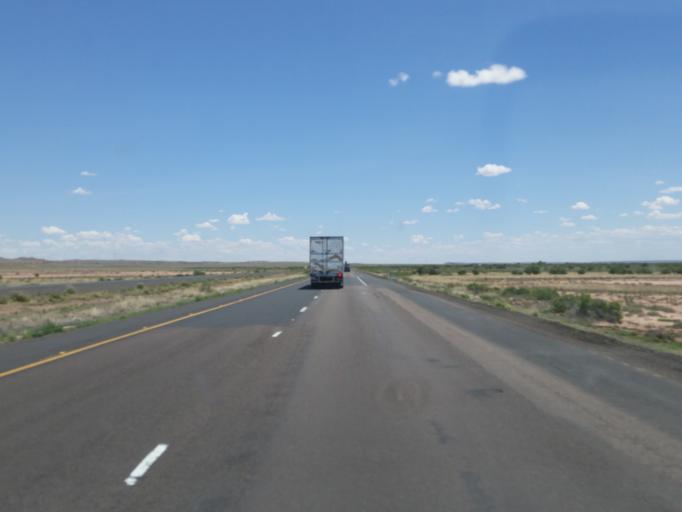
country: US
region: Arizona
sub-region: Navajo County
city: Winslow
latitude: 34.9946
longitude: -110.5827
